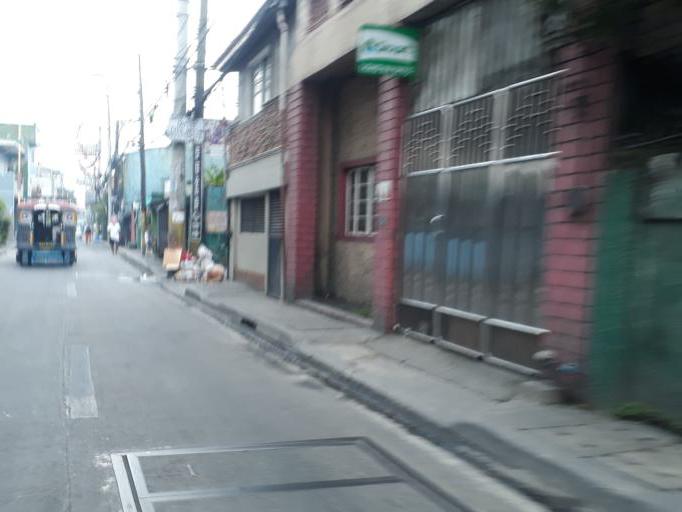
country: PH
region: Calabarzon
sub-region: Province of Rizal
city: Navotas
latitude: 14.6575
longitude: 120.9461
